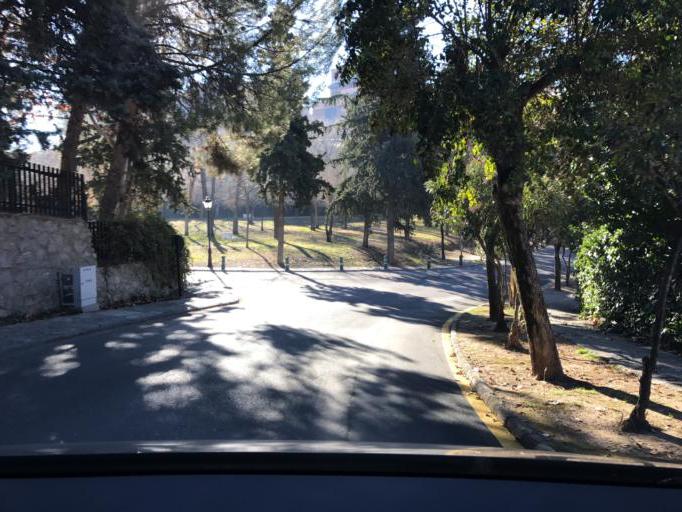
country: ES
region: Andalusia
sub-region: Provincia de Granada
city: Huetor Vega
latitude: 37.1605
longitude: -3.5787
